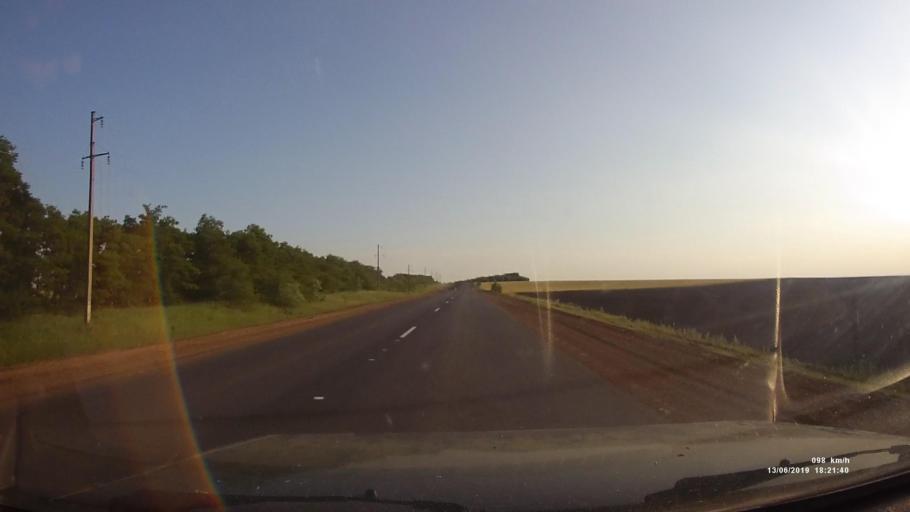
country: RU
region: Rostov
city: Kazanskaya
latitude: 49.8681
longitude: 41.2879
